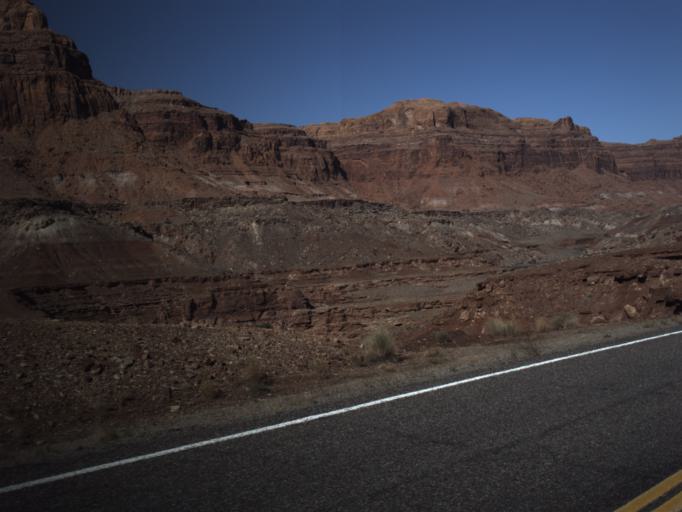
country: US
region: Utah
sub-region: San Juan County
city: Blanding
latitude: 37.8848
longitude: -110.4272
